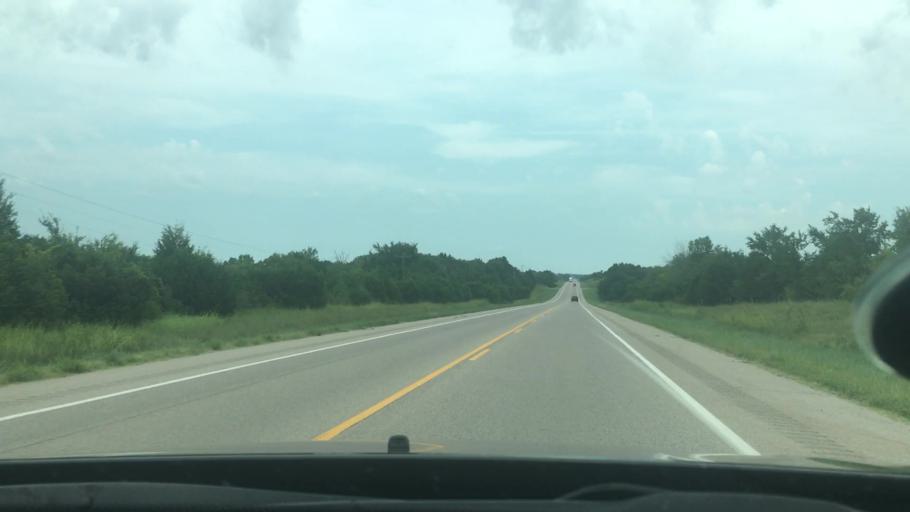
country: US
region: Oklahoma
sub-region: Seminole County
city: Konawa
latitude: 34.9876
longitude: -96.6793
